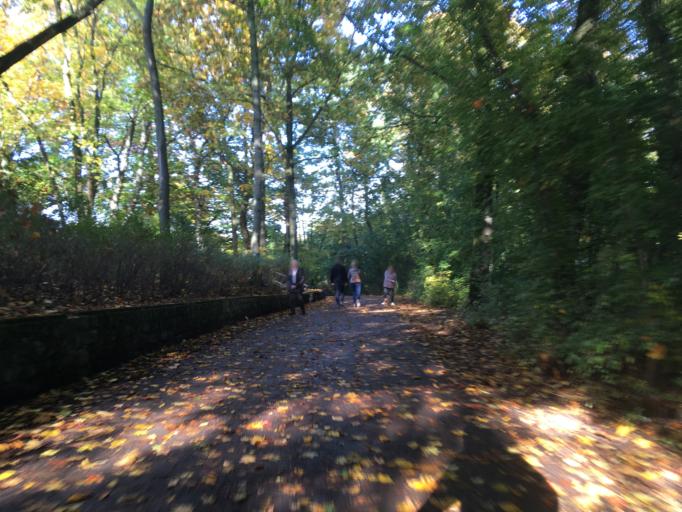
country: DE
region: Berlin
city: Berlin Koepenick
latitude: 52.4533
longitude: 13.5850
